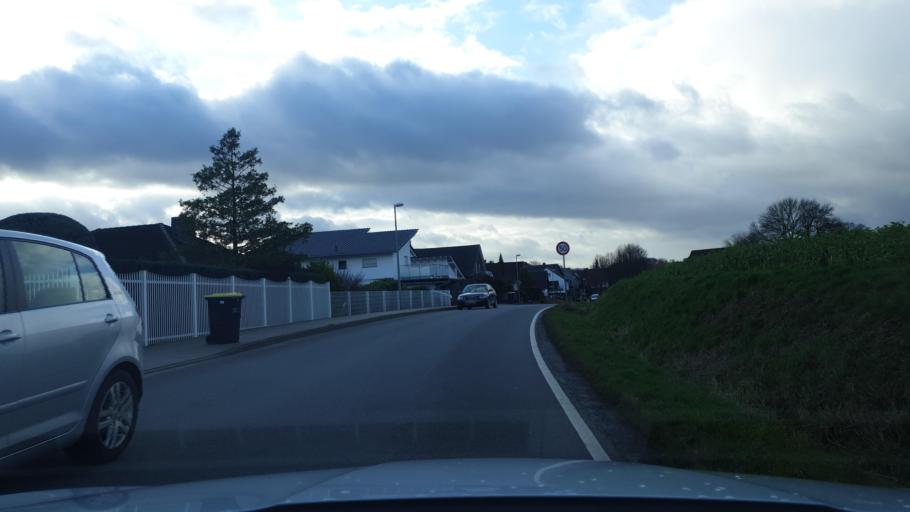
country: DE
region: North Rhine-Westphalia
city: Bad Oeynhausen
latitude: 52.1980
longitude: 8.8373
